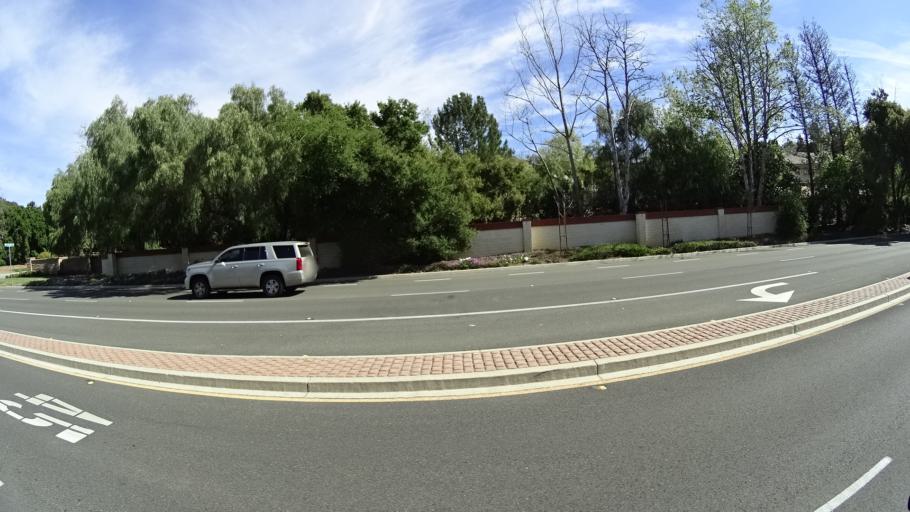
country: US
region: California
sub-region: Ventura County
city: Oak Park
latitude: 34.1909
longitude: -118.7929
